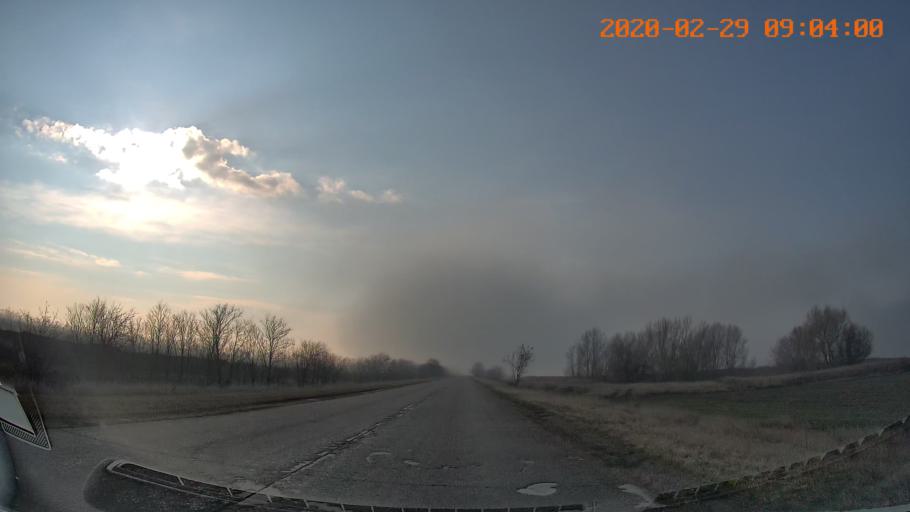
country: UA
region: Odessa
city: Velykoploske
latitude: 46.9086
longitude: 29.7341
